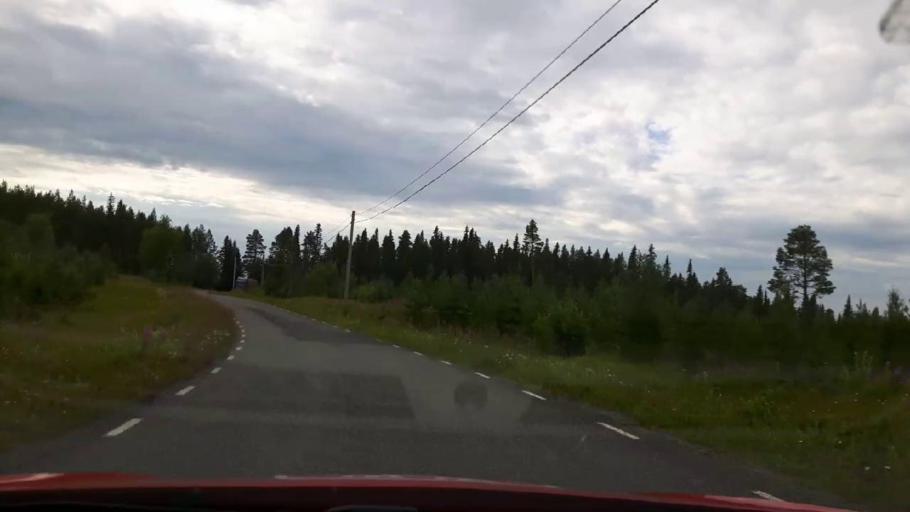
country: SE
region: Jaemtland
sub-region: OEstersunds Kommun
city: Lit
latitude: 63.3919
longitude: 15.0117
